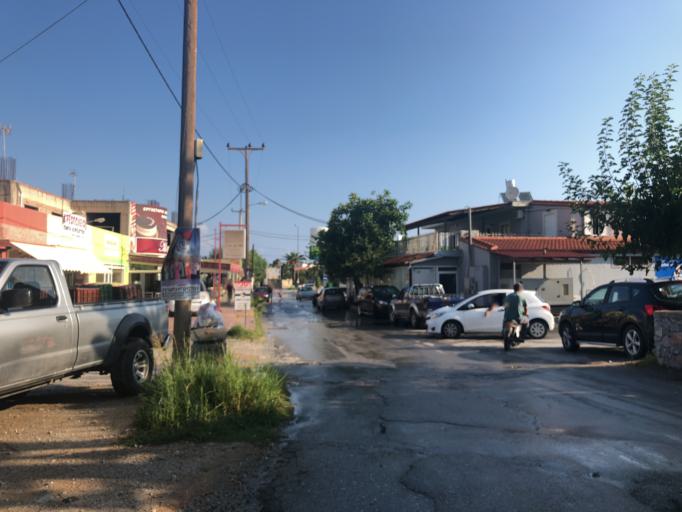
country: GR
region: Crete
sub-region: Nomos Chanias
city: Georgioupolis
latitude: 35.3501
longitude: 24.3013
